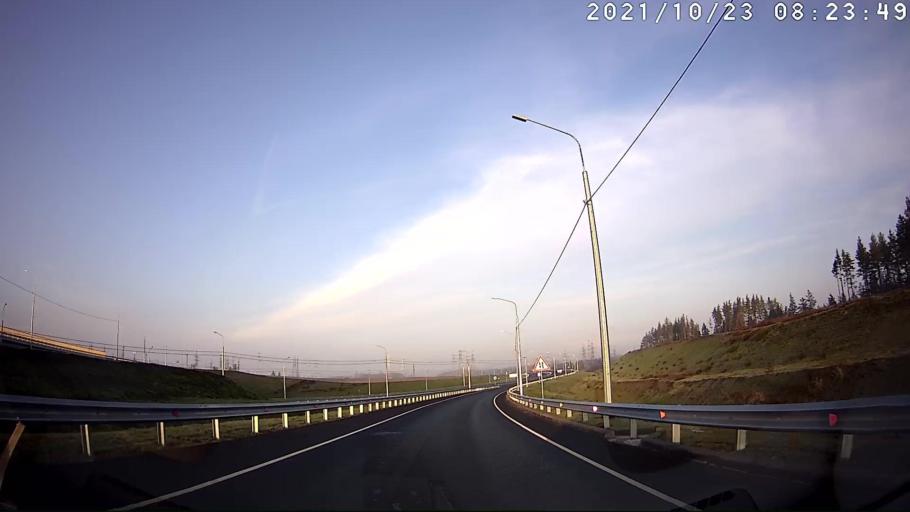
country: RU
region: Saratov
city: Sennoy
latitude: 52.1427
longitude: 46.9173
